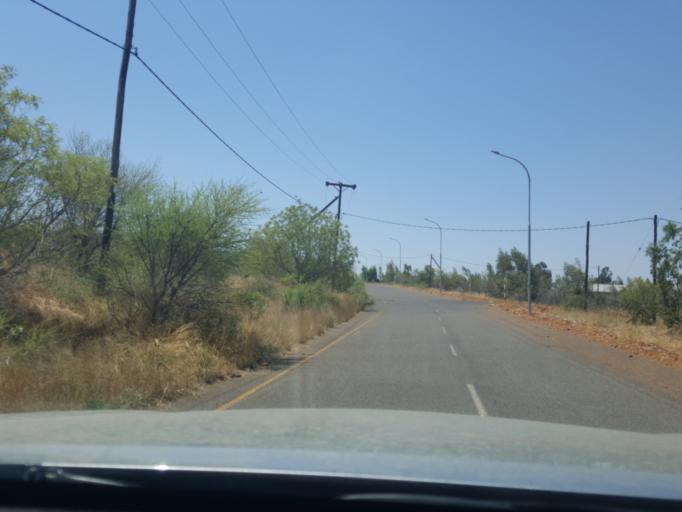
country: BW
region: South East
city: Lobatse
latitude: -25.1829
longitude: 25.6808
